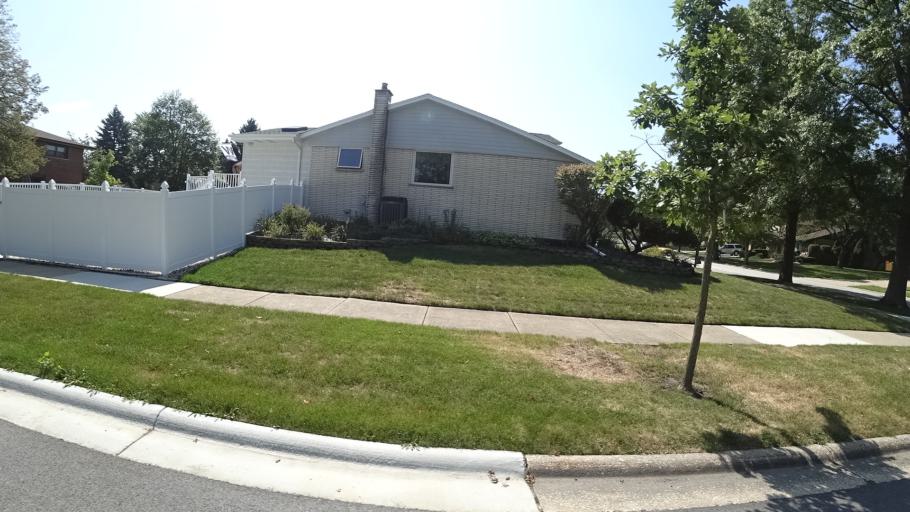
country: US
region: Illinois
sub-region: Cook County
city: Oak Forest
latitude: 41.6119
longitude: -87.7799
